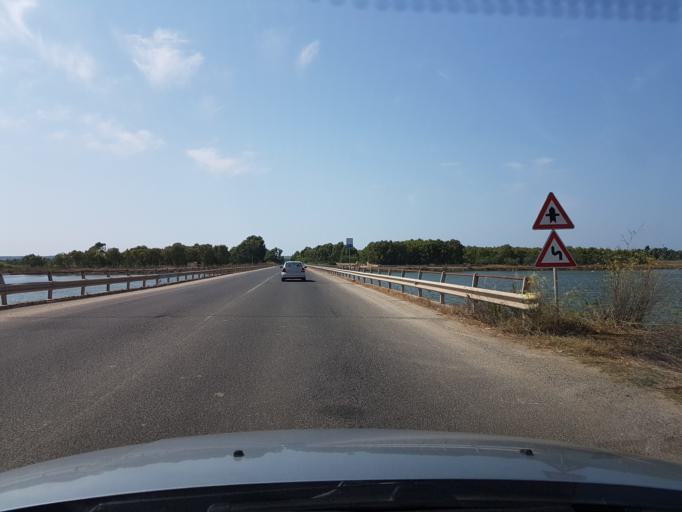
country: IT
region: Sardinia
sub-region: Provincia di Oristano
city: Cabras
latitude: 39.9166
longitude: 8.4993
